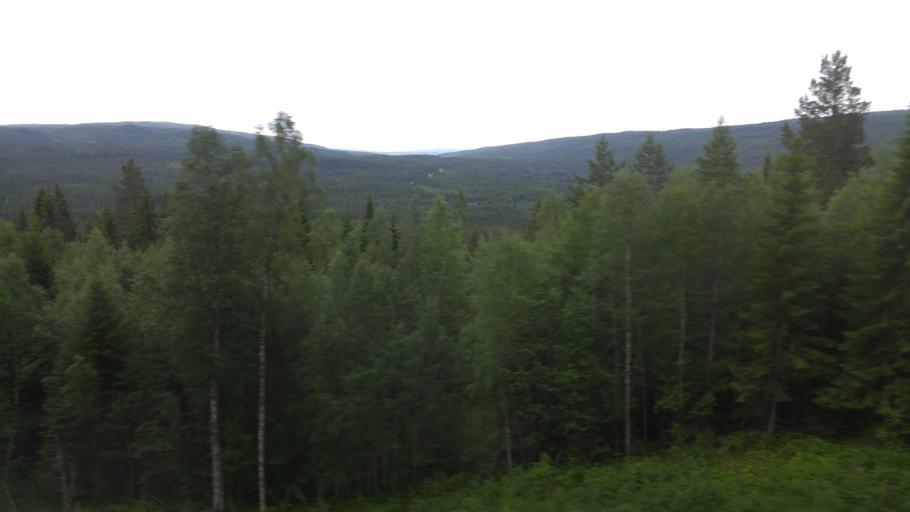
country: NO
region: Nord-Trondelag
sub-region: Meraker
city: Meraker
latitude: 63.4000
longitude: 11.8084
